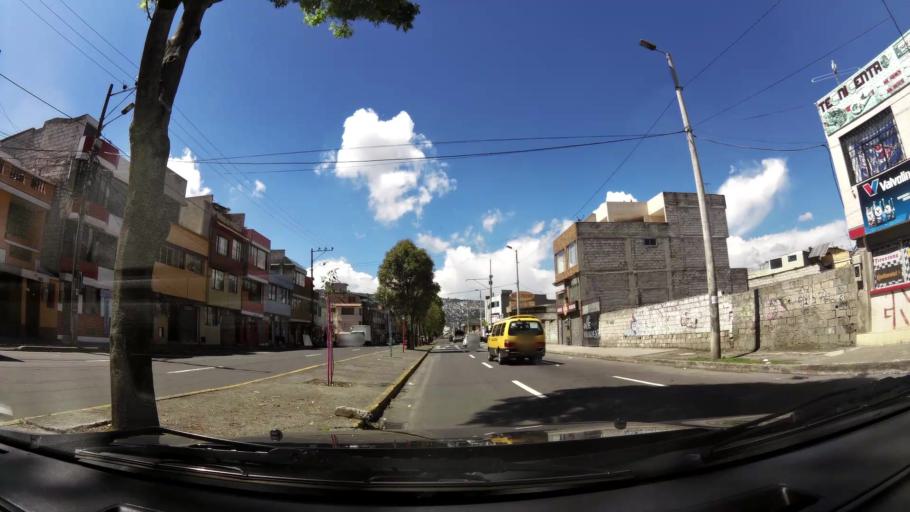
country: EC
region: Pichincha
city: Quito
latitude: -0.2712
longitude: -78.5439
